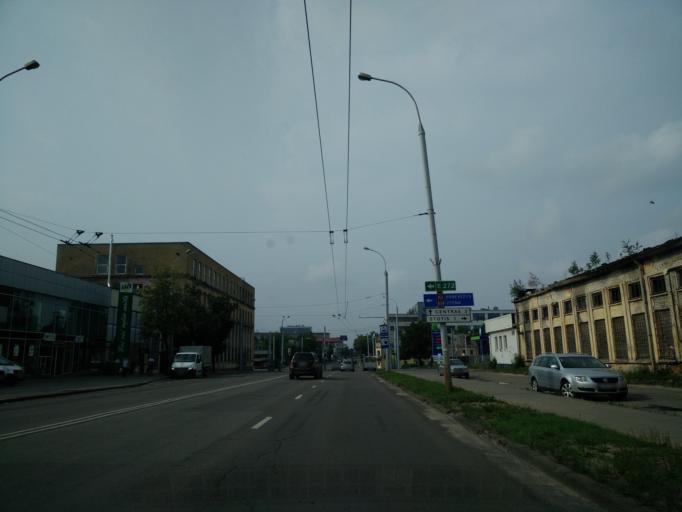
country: LT
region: Vilnius County
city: Naujamiestis
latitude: 54.6706
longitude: 25.2700
